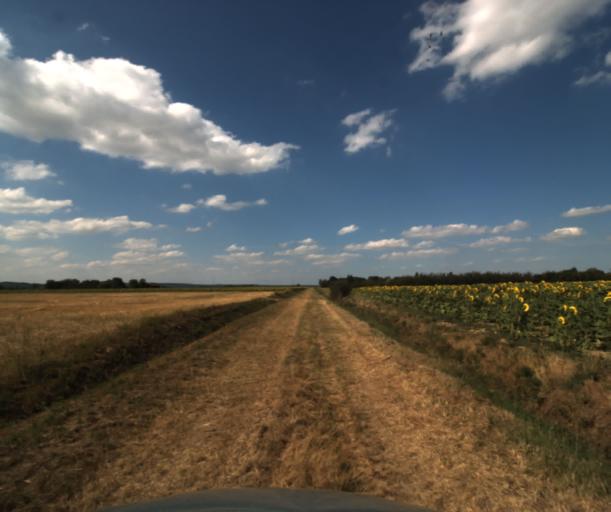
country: FR
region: Midi-Pyrenees
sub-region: Departement de la Haute-Garonne
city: Saint-Lys
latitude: 43.5258
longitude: 1.1786
